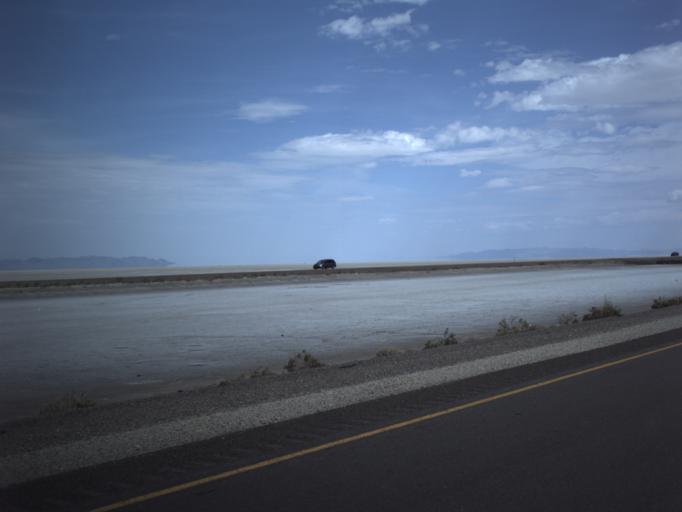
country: US
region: Utah
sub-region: Tooele County
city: Wendover
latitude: 40.7352
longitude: -113.6925
